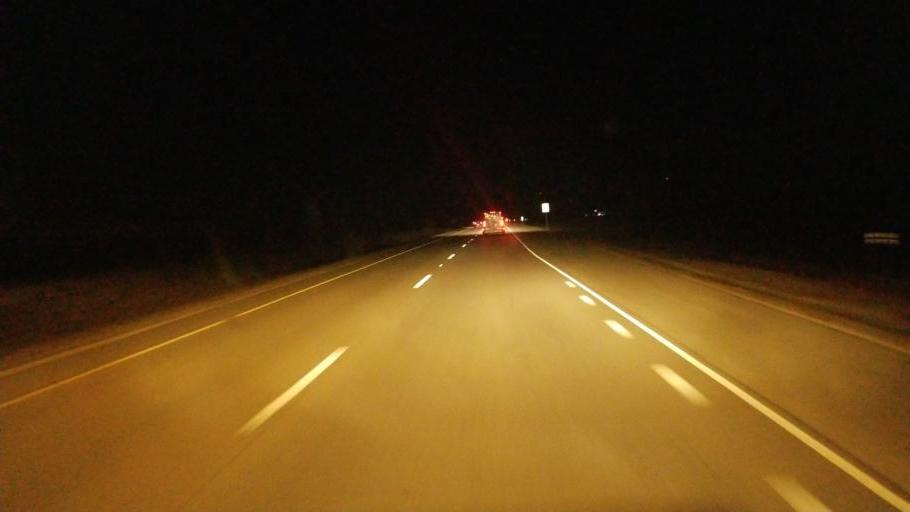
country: US
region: Illinois
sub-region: Henderson County
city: Oquawka
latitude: 40.8465
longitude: -90.9118
